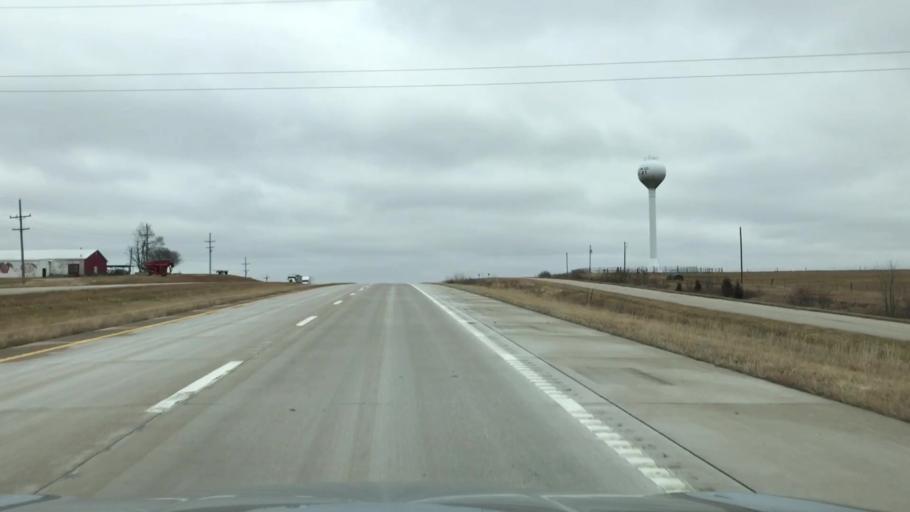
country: US
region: Missouri
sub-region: Livingston County
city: Chillicothe
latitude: 39.7393
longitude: -93.6614
